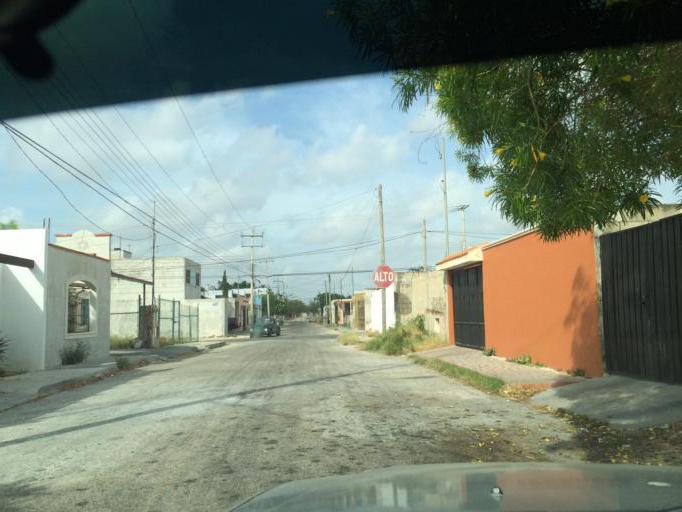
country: MX
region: Yucatan
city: Merida
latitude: 20.9939
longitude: -89.5752
